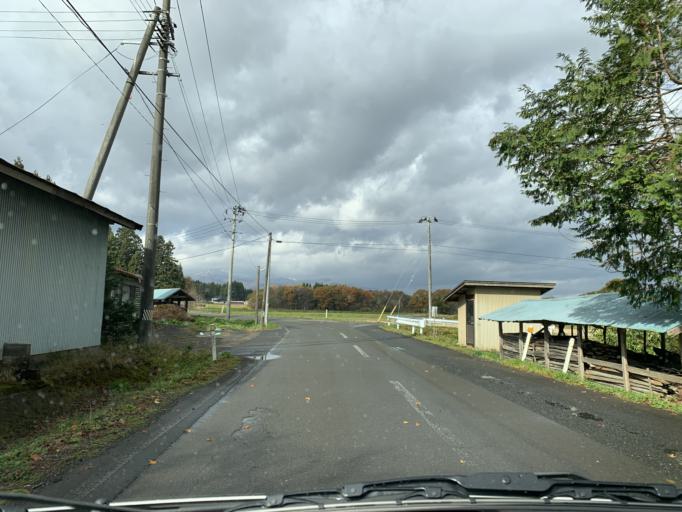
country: JP
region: Iwate
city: Mizusawa
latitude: 39.0904
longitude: 141.0174
